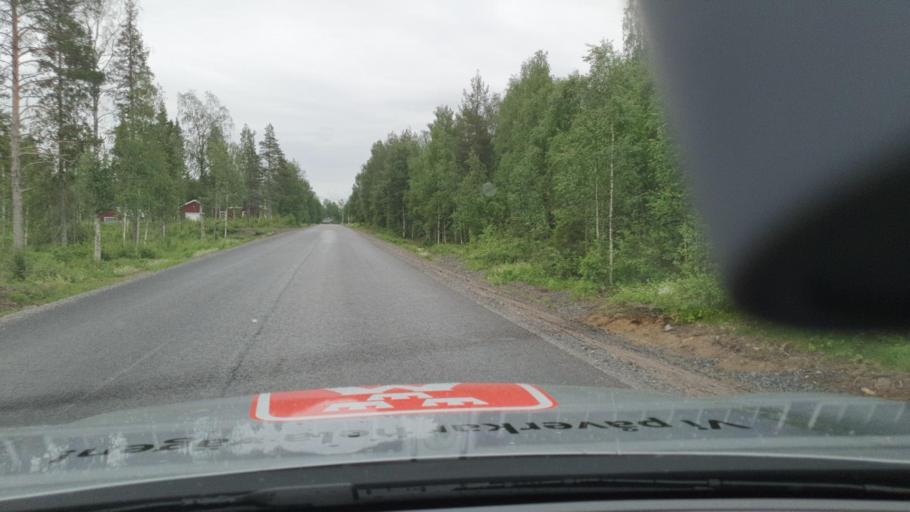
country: SE
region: Norrbotten
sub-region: Pajala Kommun
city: Pajala
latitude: 66.7356
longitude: 23.1700
